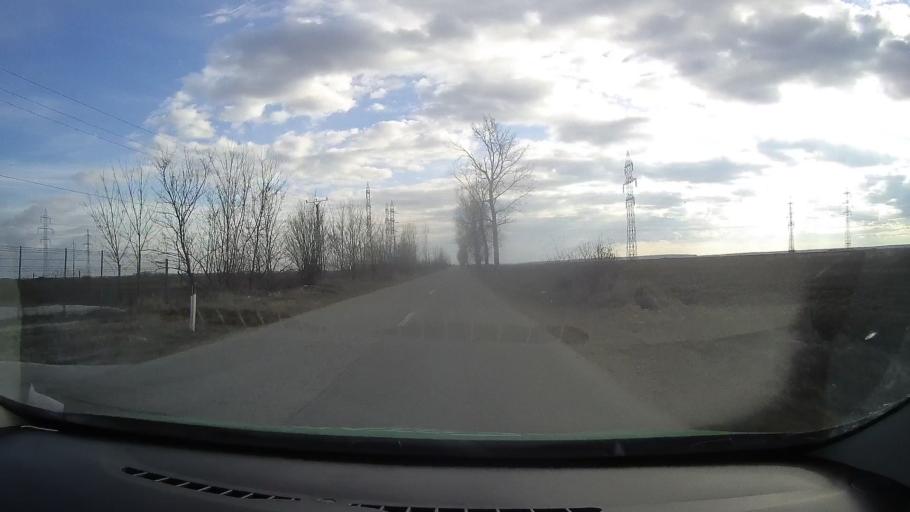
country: RO
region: Dambovita
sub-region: Comuna Ulmi
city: Viisoara
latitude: 44.8814
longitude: 25.4641
